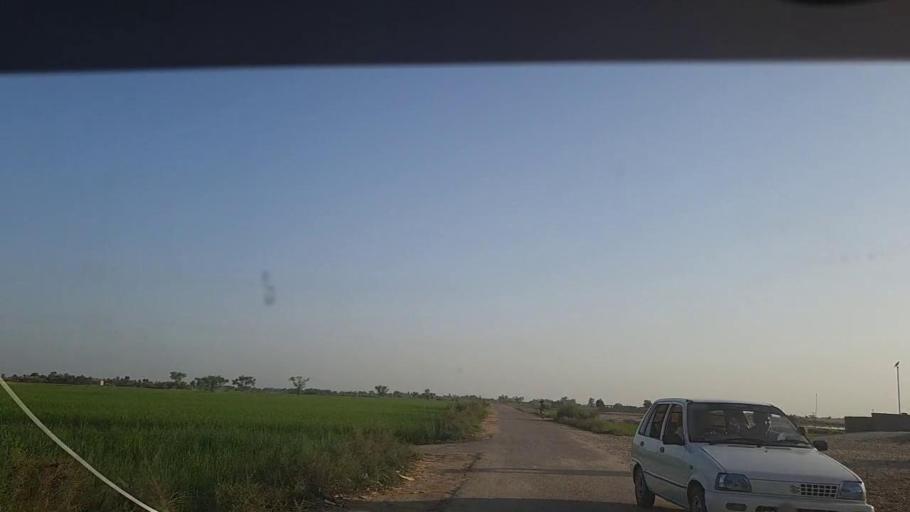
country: PK
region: Sindh
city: Thul
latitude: 28.1954
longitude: 68.8733
